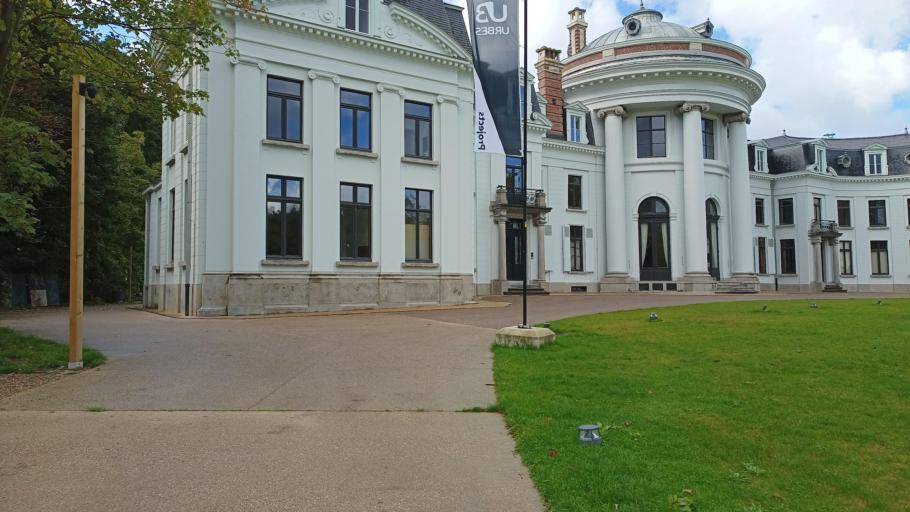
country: BE
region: Flanders
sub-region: Provincie West-Vlaanderen
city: Izegem
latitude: 50.9183
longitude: 3.2229
